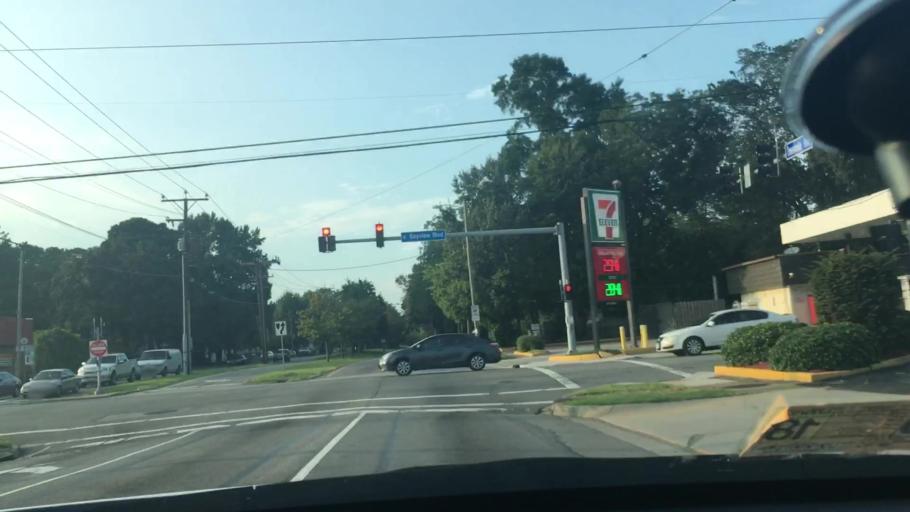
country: US
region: Virginia
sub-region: City of Norfolk
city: Norfolk
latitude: 36.9336
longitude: -76.2443
